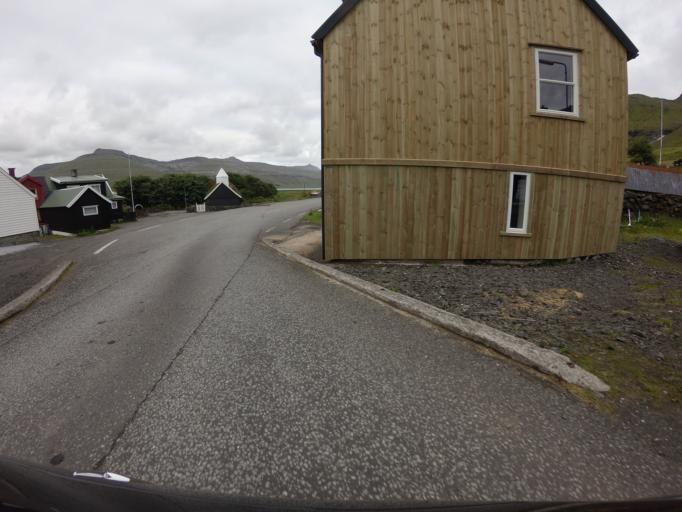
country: FO
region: Eysturoy
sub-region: Eidi
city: Eidi
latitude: 62.1872
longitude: -7.0371
